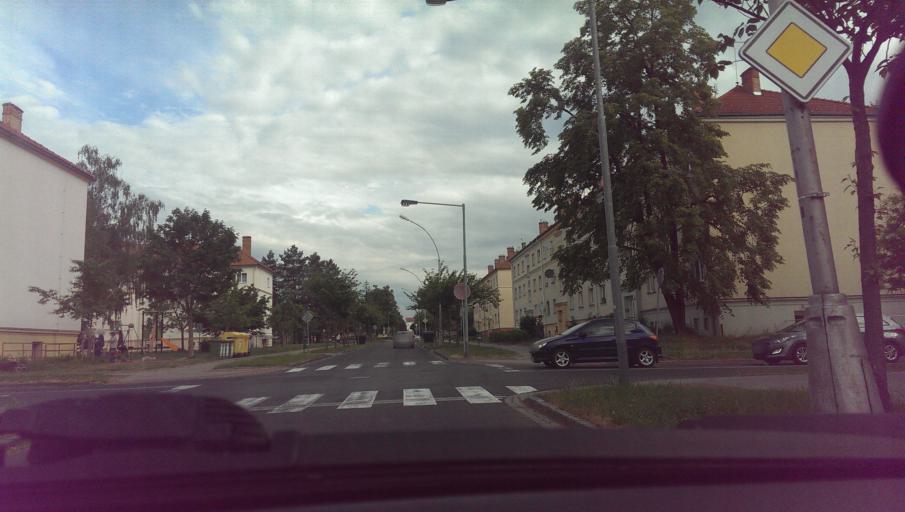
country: CZ
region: Zlin
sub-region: Okres Kromeriz
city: Kromeriz
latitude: 49.2906
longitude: 17.3929
